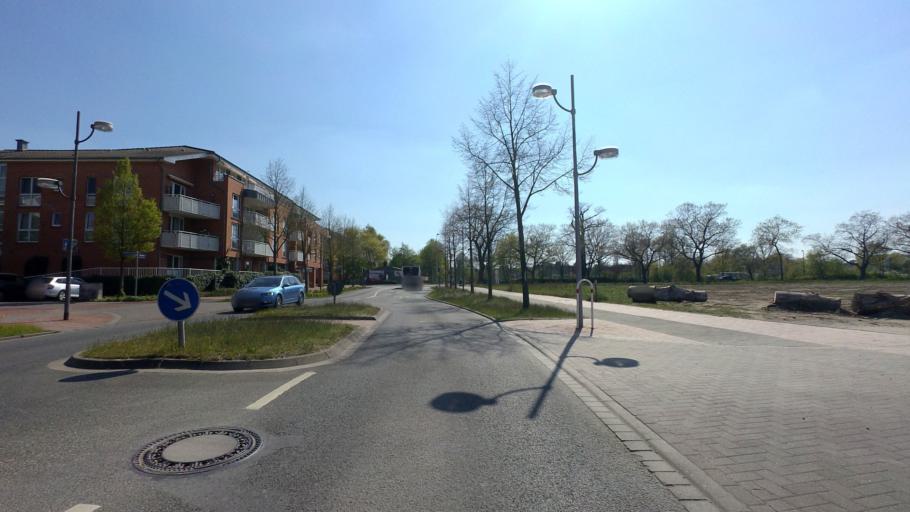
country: DE
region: Lower Saxony
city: Celle
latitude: 52.6185
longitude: 10.0859
